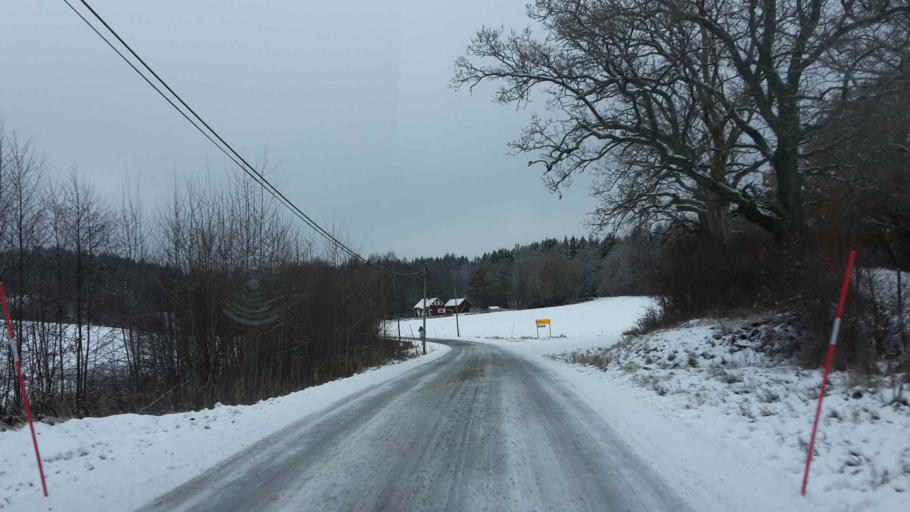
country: SE
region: Kalmar
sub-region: Vasterviks Kommun
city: Overum
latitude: 58.1534
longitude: 16.3049
